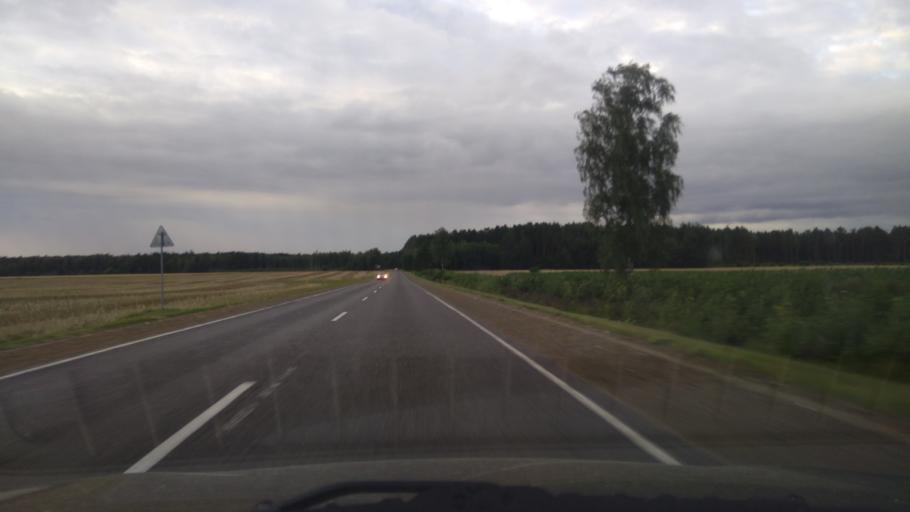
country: BY
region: Brest
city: Byaroza
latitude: 52.3997
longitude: 25.0043
